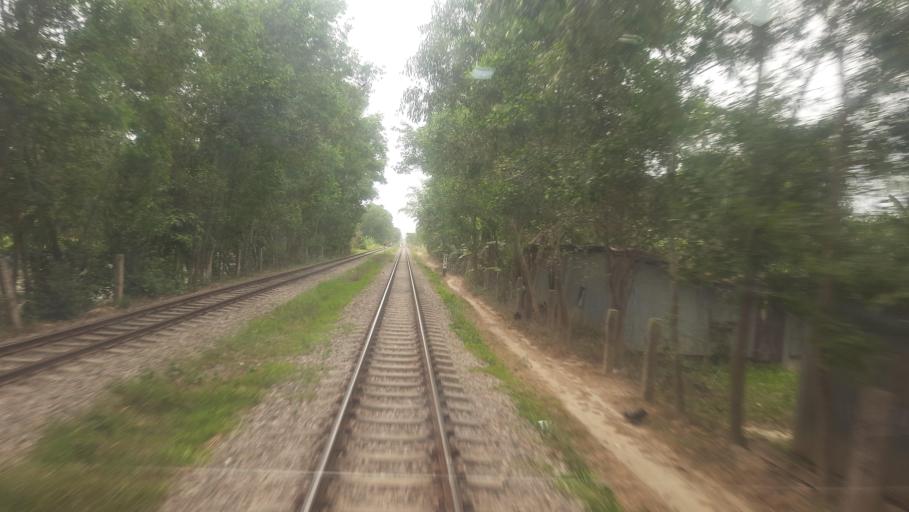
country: BD
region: Chittagong
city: Feni
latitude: 23.0287
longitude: 91.3817
